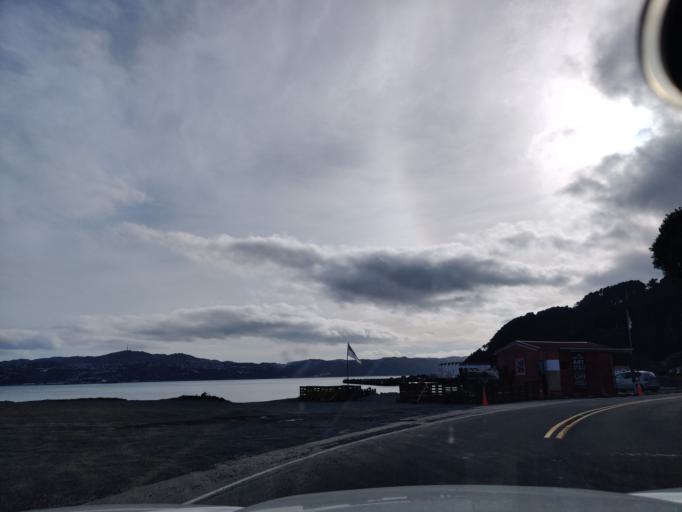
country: NZ
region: Wellington
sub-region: Wellington City
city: Wellington
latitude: -41.2977
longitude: 174.8207
